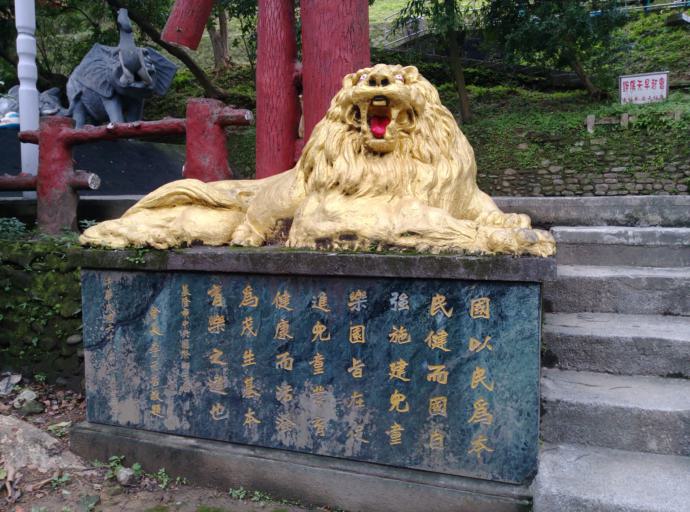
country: TW
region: Taiwan
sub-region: Keelung
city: Keelung
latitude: 25.1313
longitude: 121.7474
